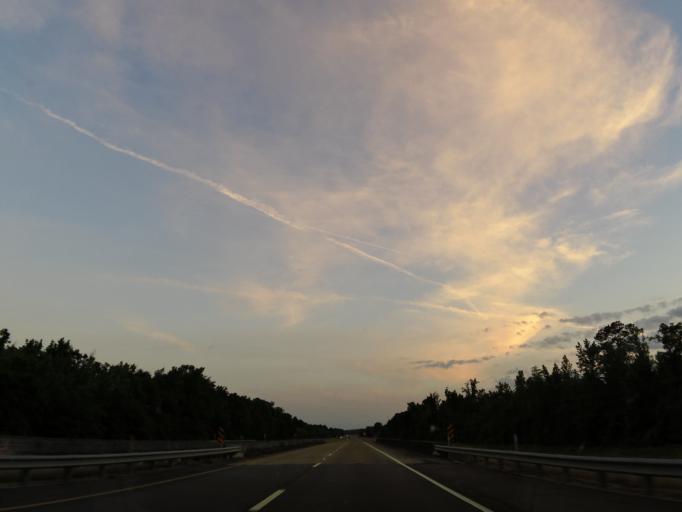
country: US
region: Mississippi
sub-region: Kemper County
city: De Kalb
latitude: 32.7047
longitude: -88.4834
